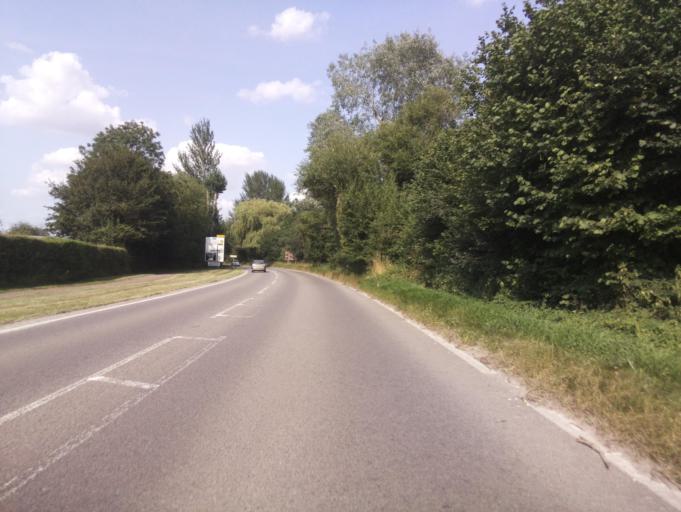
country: GB
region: England
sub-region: Wiltshire
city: Leigh
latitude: 51.6572
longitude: -1.9171
